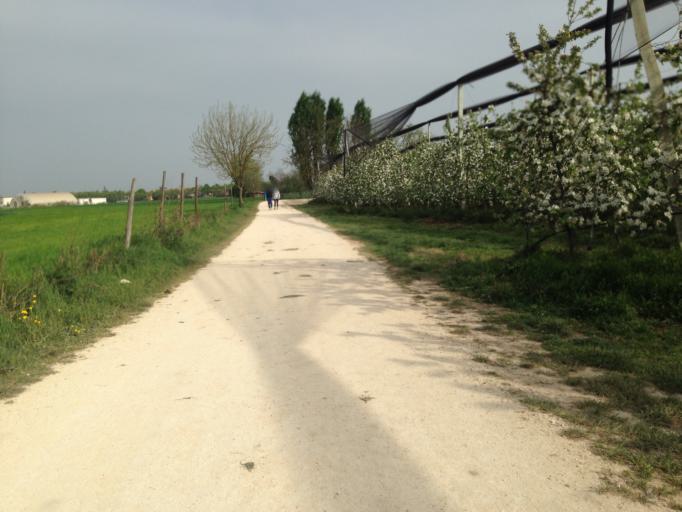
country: IT
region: Veneto
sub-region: Provincia di Verona
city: Zevio
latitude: 45.3770
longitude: 11.1185
